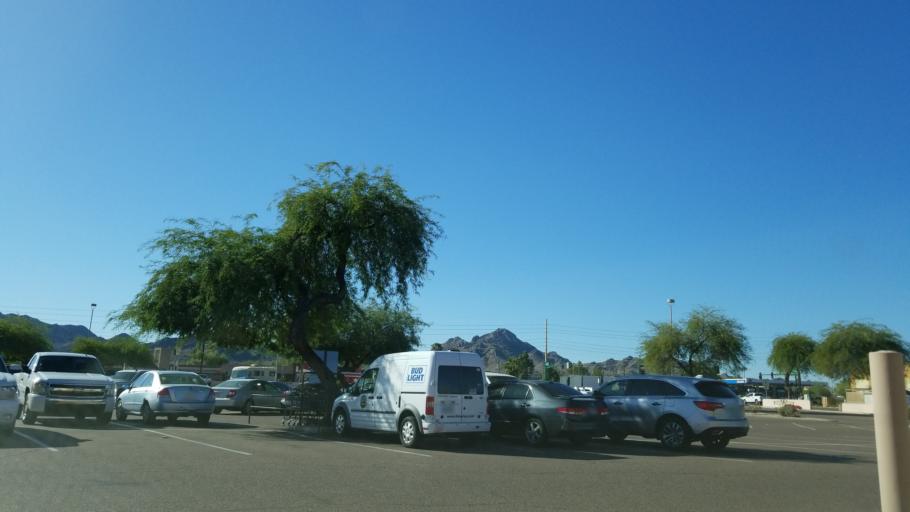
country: US
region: Arizona
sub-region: Maricopa County
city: Paradise Valley
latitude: 33.5838
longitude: -112.0123
